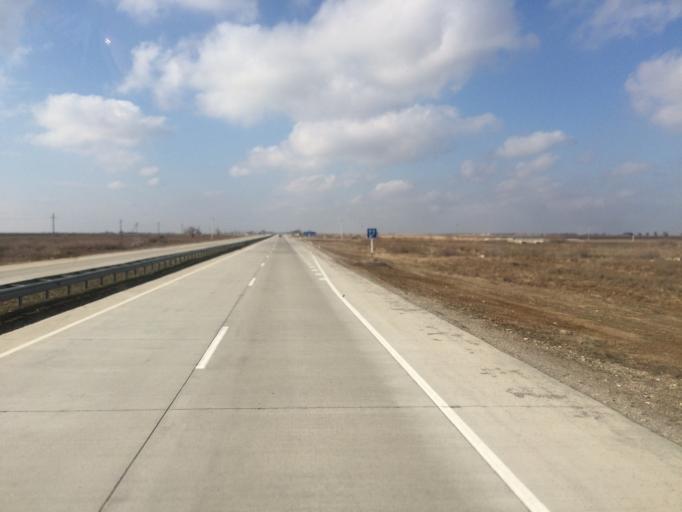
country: KZ
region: Ongtustik Qazaqstan
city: Shayan
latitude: 42.9794
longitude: 68.8465
